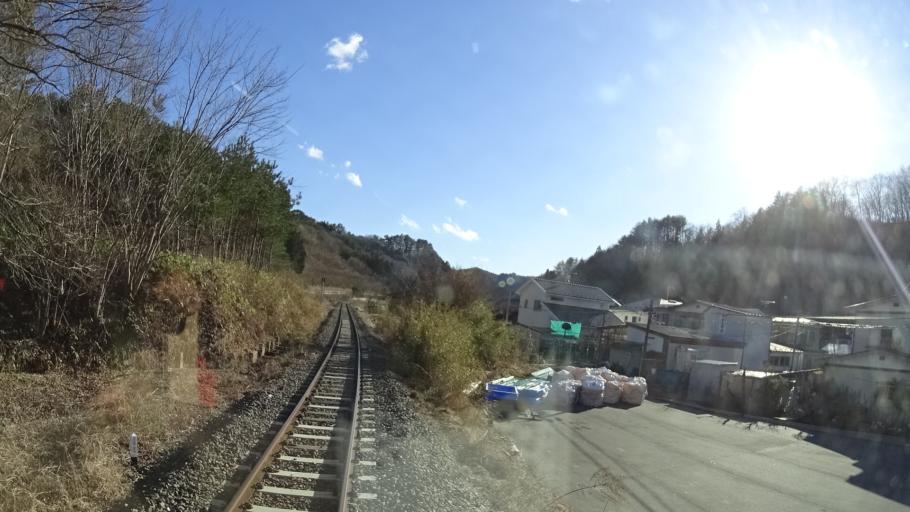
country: JP
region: Iwate
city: Miyako
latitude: 39.6138
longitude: 141.9388
